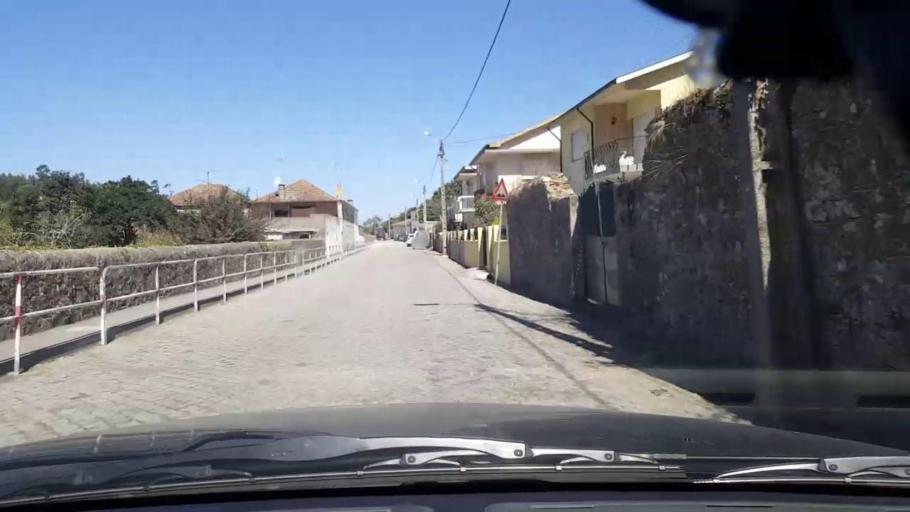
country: PT
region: Porto
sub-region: Maia
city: Gemunde
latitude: 41.3336
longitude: -8.6455
